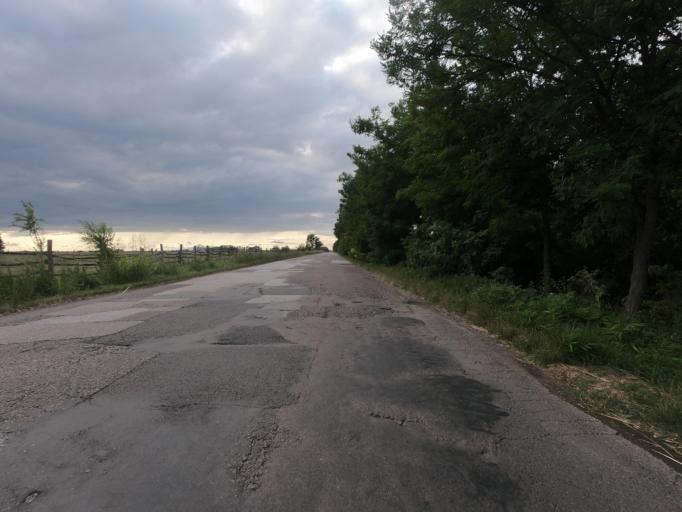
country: HU
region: Heves
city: Poroszlo
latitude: 47.6736
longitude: 20.6597
